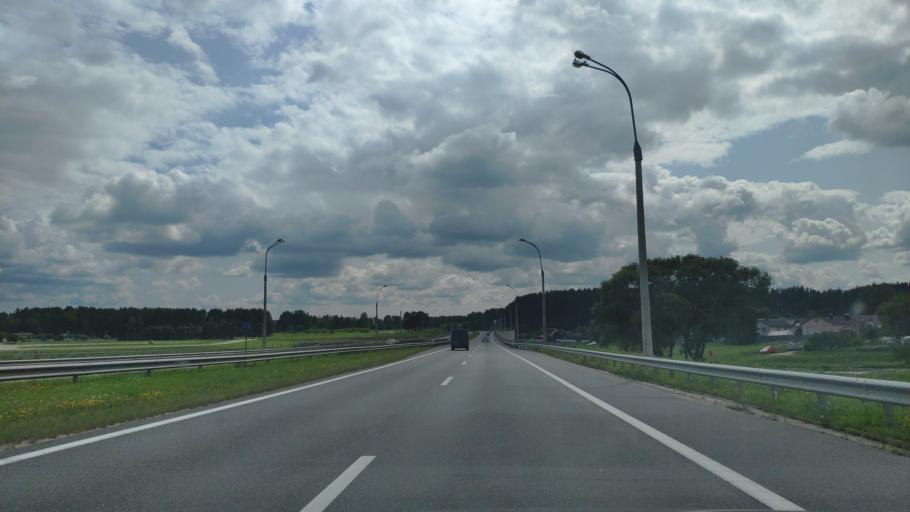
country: BY
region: Minsk
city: Zaslawye
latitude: 53.9983
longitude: 27.3068
